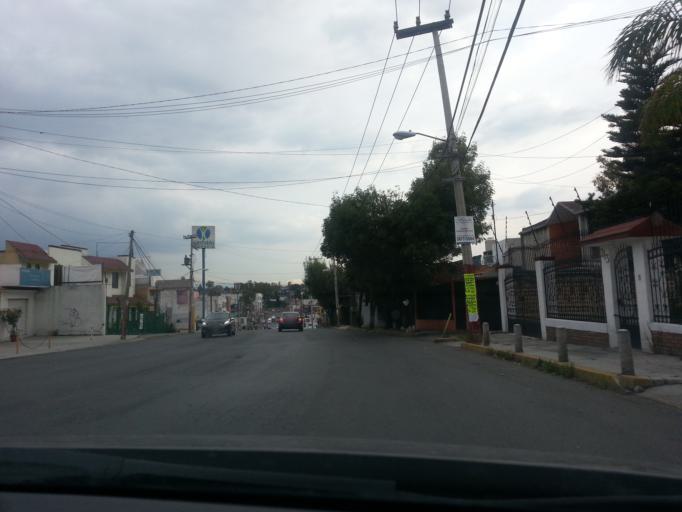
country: MX
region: Mexico
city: Ciudad Lopez Mateos
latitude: 19.6161
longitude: -99.2400
